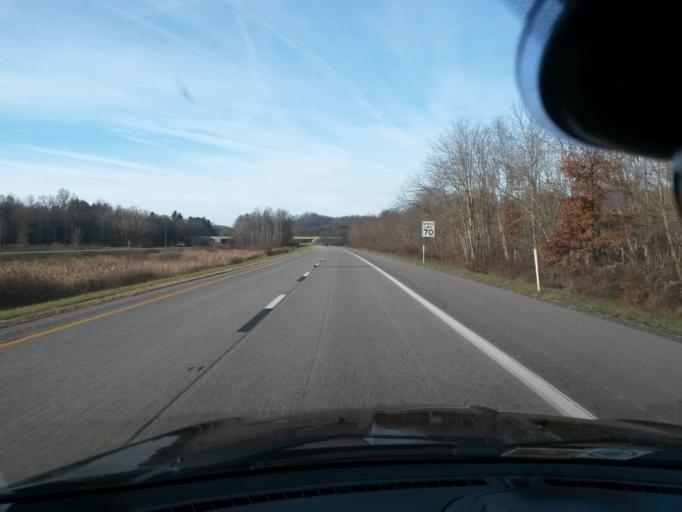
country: US
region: West Virginia
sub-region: Greenbrier County
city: Rainelle
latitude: 37.9007
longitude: -80.6450
